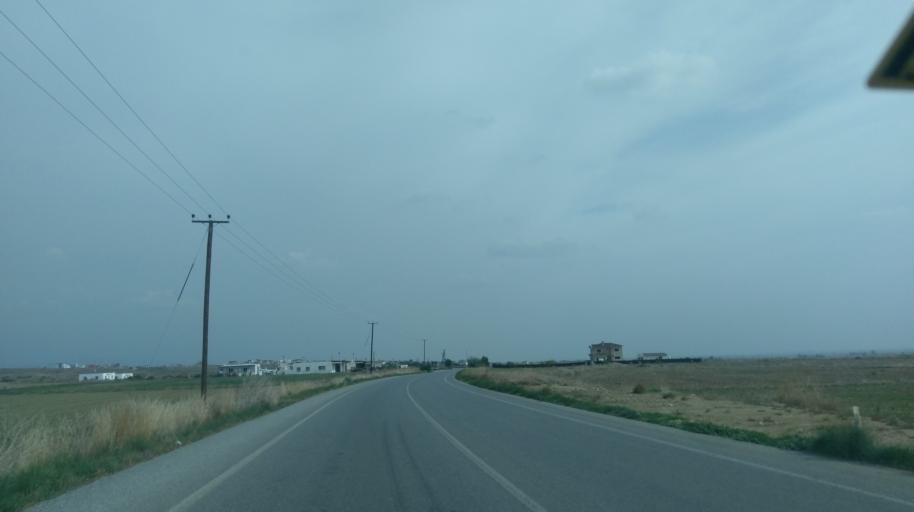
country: CY
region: Ammochostos
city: Lefkonoiko
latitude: 35.2397
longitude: 33.5841
